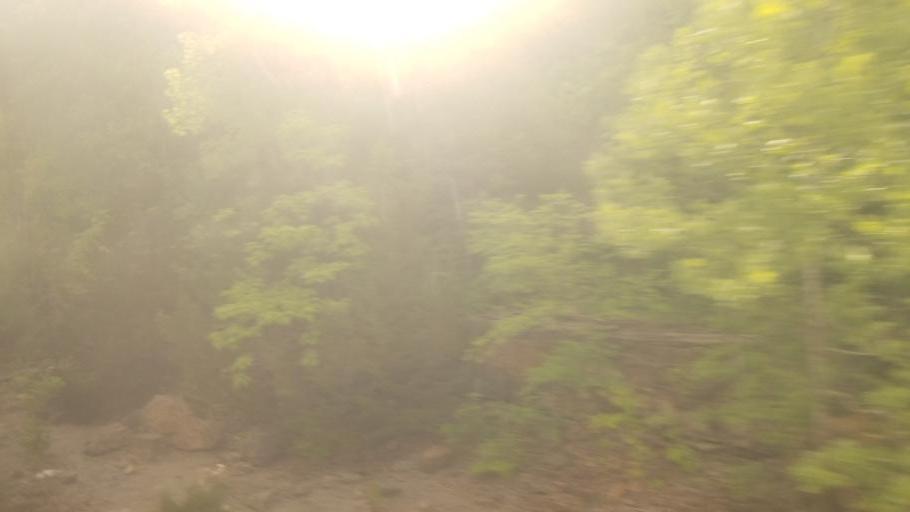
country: US
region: Kansas
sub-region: Johnson County
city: De Soto
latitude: 38.9833
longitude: -94.9168
